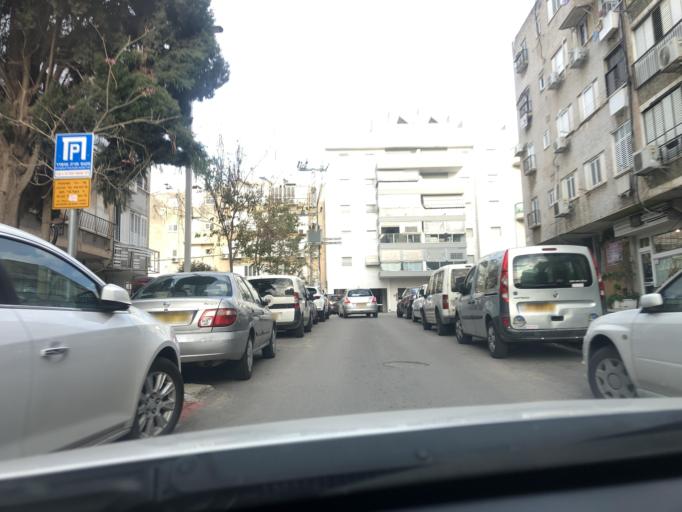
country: IL
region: Tel Aviv
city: Bat Yam
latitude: 32.0226
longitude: 34.7541
